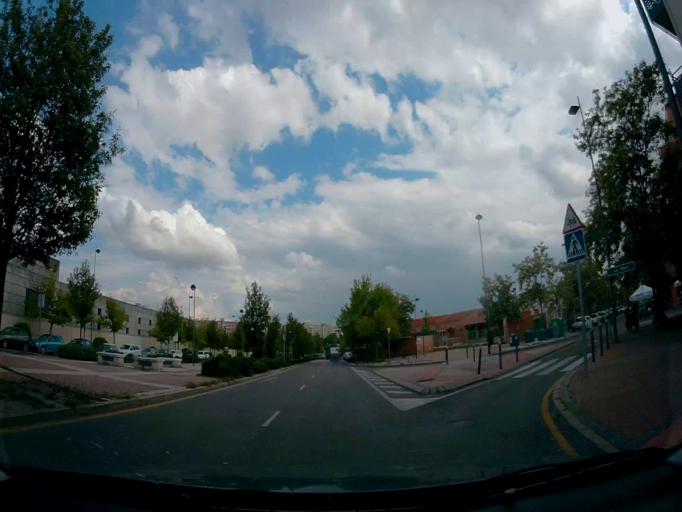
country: ES
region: Madrid
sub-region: Provincia de Madrid
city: Alcorcon
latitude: 40.3472
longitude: -3.8395
